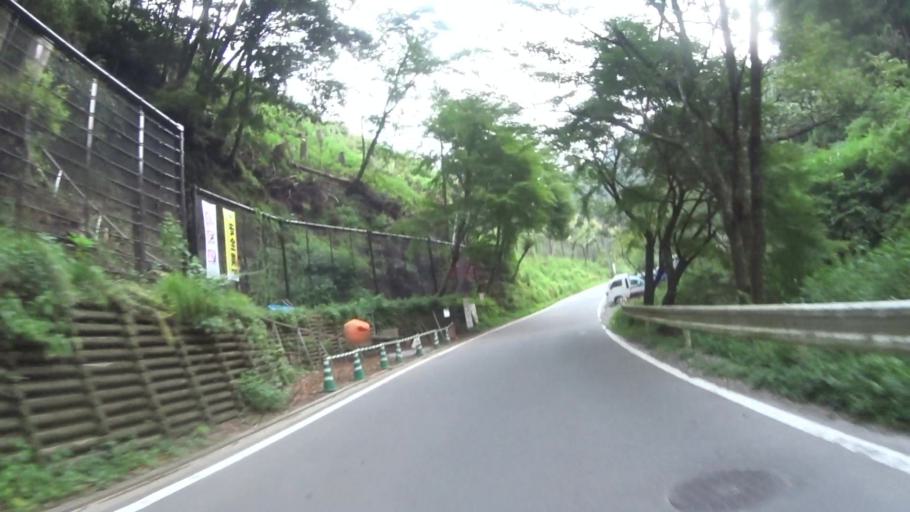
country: JP
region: Kyoto
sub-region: Kyoto-shi
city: Kamigyo-ku
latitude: 35.1182
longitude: 135.7614
